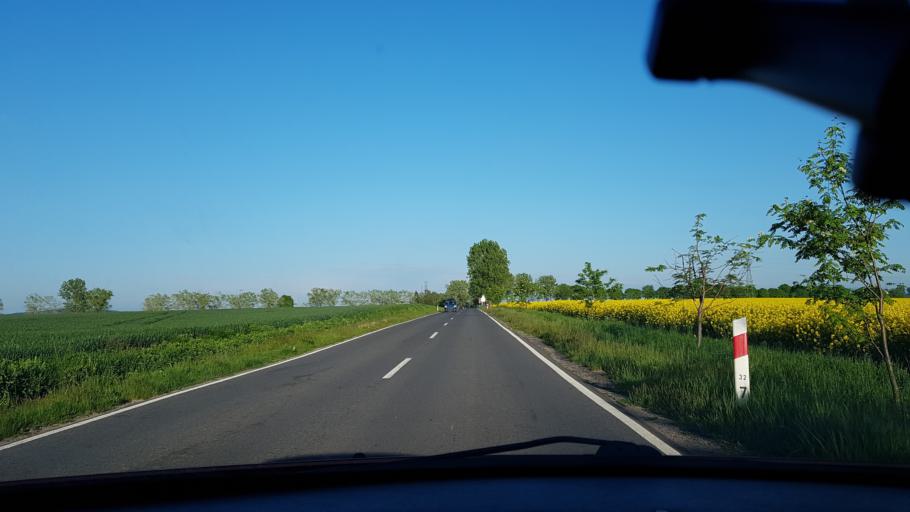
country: PL
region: Lower Silesian Voivodeship
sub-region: Powiat zabkowicki
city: Zabkowice Slaskie
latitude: 50.5954
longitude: 16.7802
